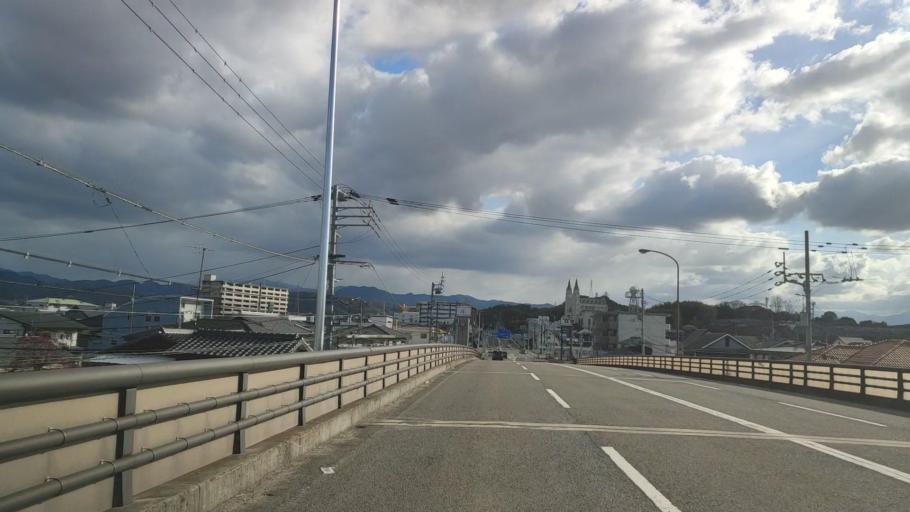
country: JP
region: Ehime
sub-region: Shikoku-chuo Shi
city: Matsuyama
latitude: 33.8571
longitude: 132.7235
